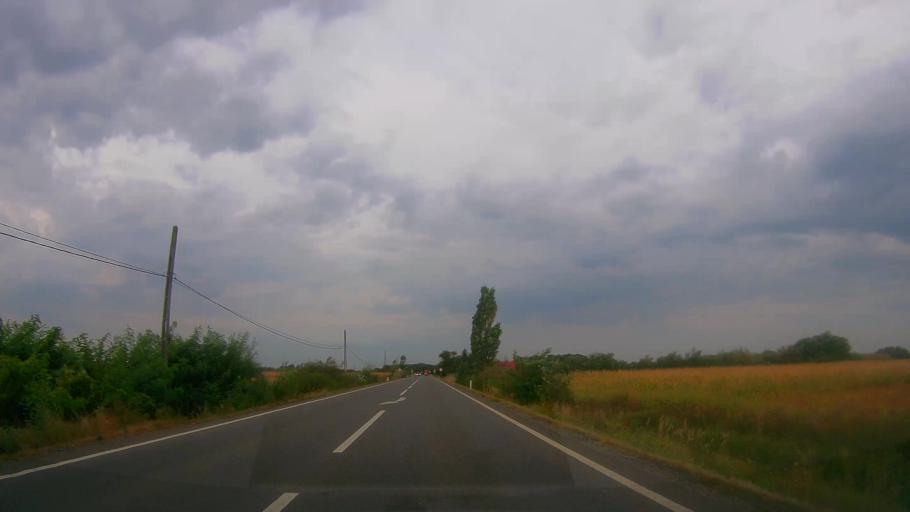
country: RO
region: Satu Mare
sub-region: Comuna Turulung
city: Draguseni
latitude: 47.8766
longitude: 23.0615
